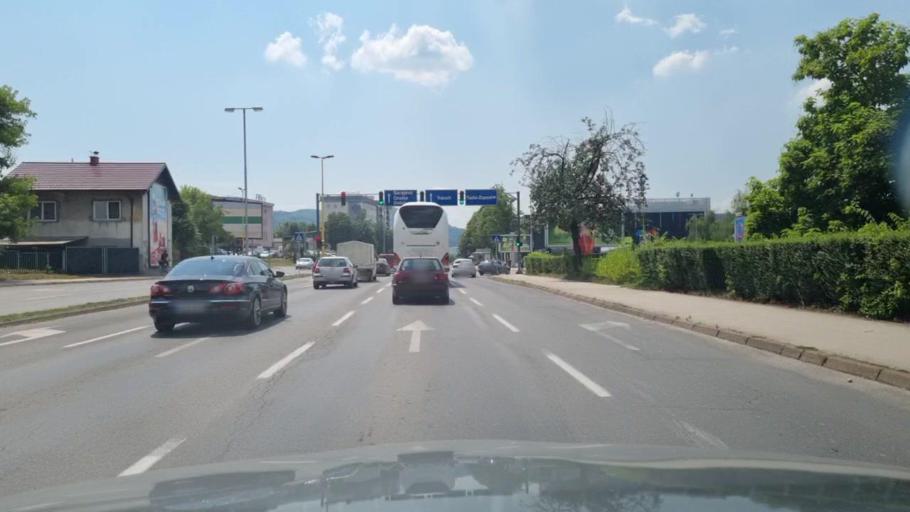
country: BA
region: Federation of Bosnia and Herzegovina
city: Tuzla
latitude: 44.5331
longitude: 18.6555
